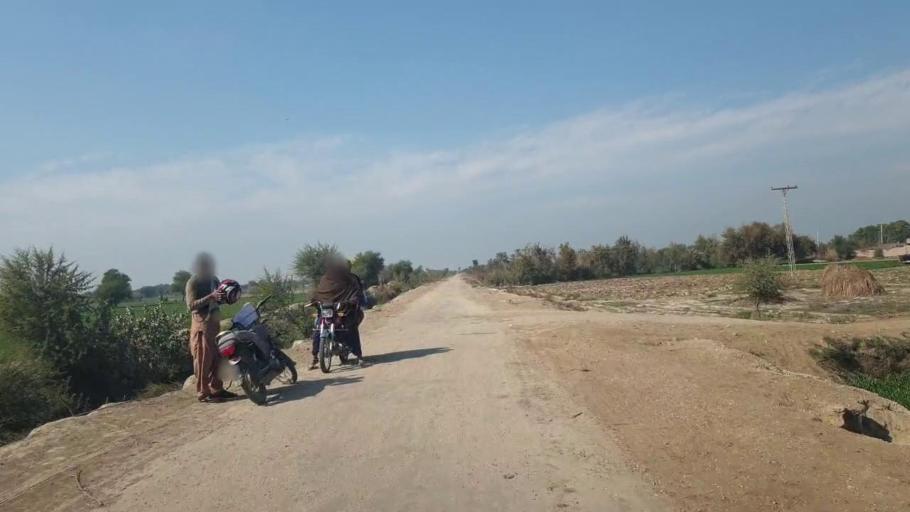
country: PK
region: Sindh
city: Shahdadpur
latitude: 25.9953
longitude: 68.5263
